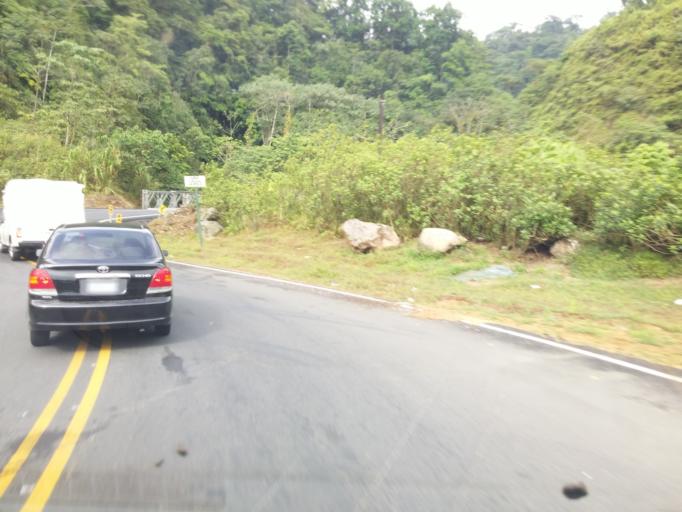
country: CR
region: Alajuela
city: San Ramon
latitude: 10.2167
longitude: -84.5446
